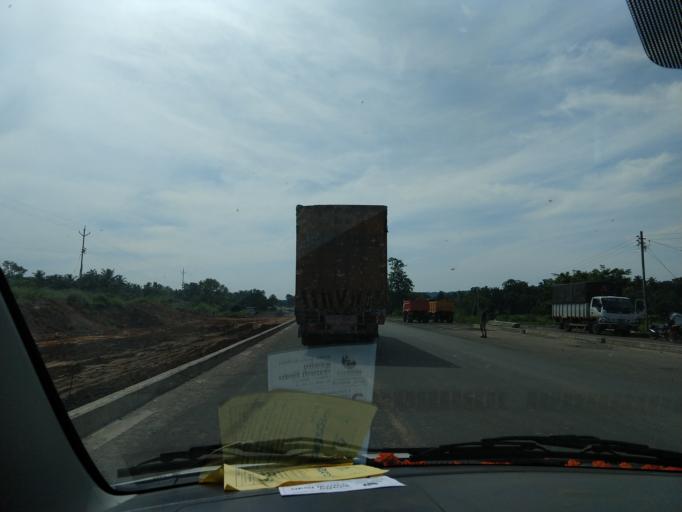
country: IN
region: Maharashtra
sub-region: Sindhudurg
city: Kudal
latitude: 15.9916
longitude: 73.6990
